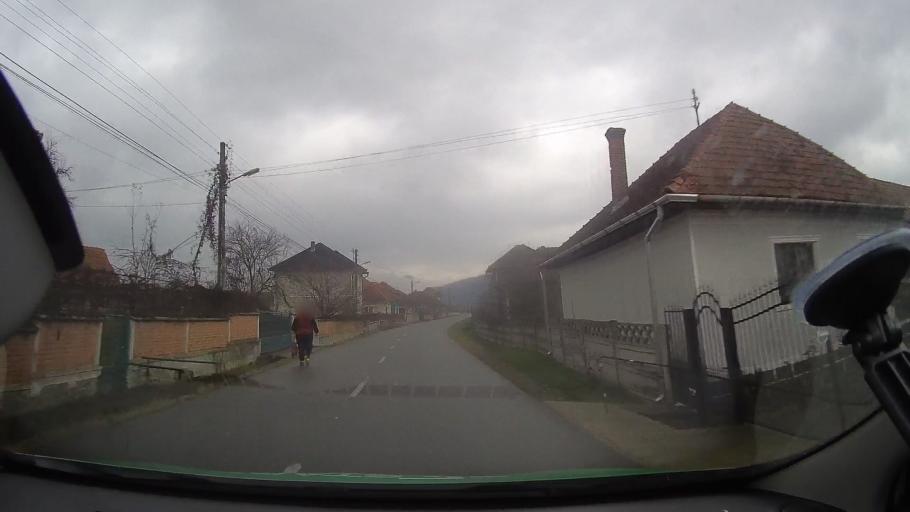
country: RO
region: Hunedoara
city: Vata de Jos
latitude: 46.1899
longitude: 22.6219
